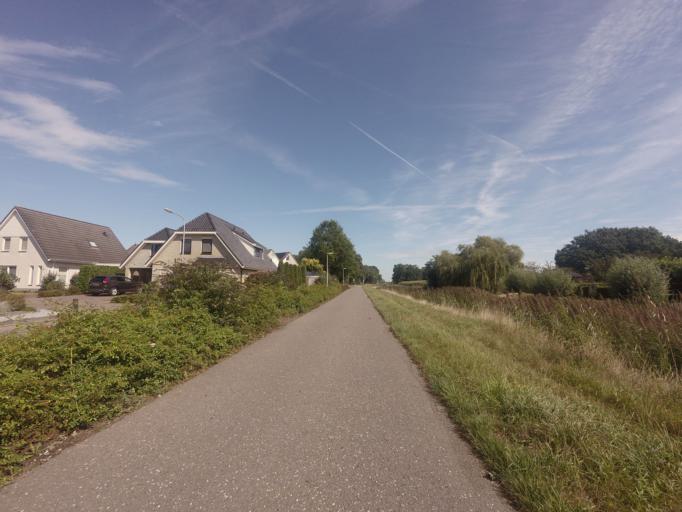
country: NL
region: Overijssel
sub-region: Gemeente Raalte
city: Raalte
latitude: 52.3979
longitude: 6.2931
